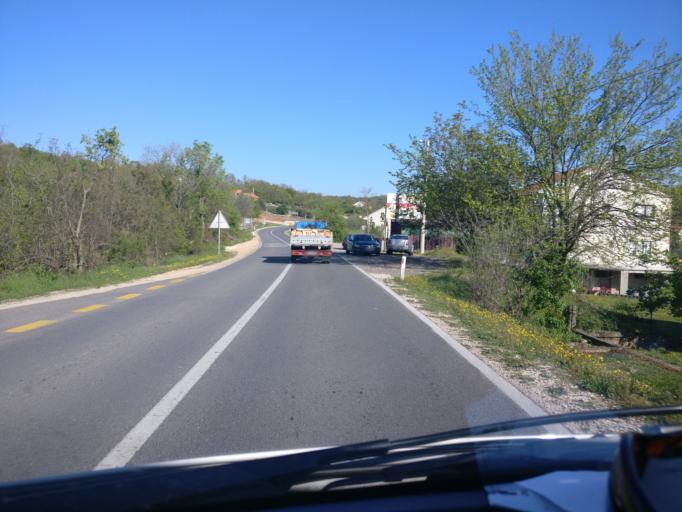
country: BA
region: Federation of Bosnia and Herzegovina
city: Crnici
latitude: 43.1059
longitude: 17.9064
